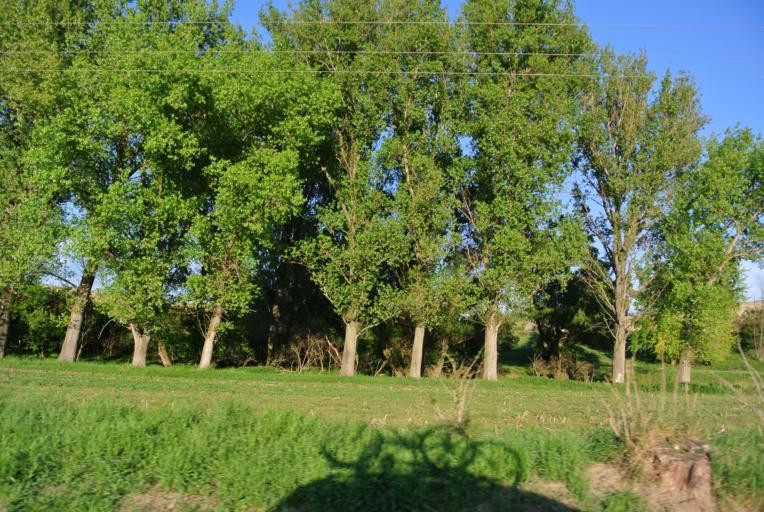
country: HU
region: Komarom-Esztergom
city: Csolnok
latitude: 47.6547
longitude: 18.7134
